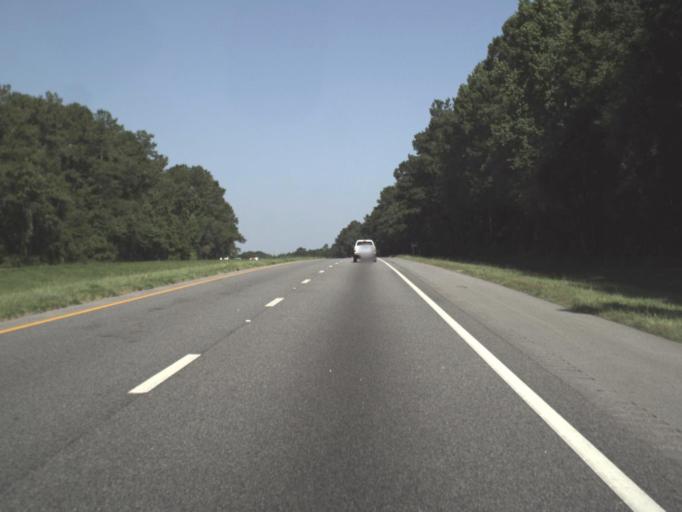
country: US
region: Florida
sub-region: Suwannee County
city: Live Oak
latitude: 30.3469
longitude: -82.9879
